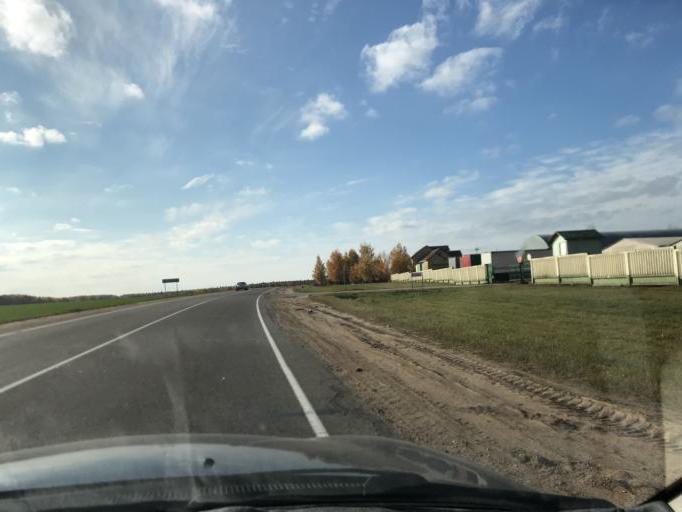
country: BY
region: Grodnenskaya
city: Voranava
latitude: 54.1441
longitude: 25.3255
